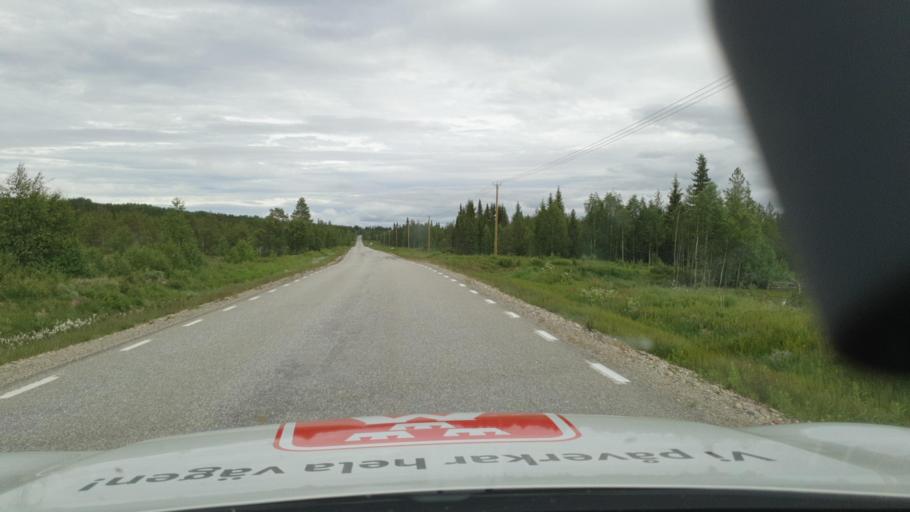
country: SE
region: Vaesterbotten
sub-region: Lycksele Kommun
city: Soderfors
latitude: 64.3679
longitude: 18.0772
